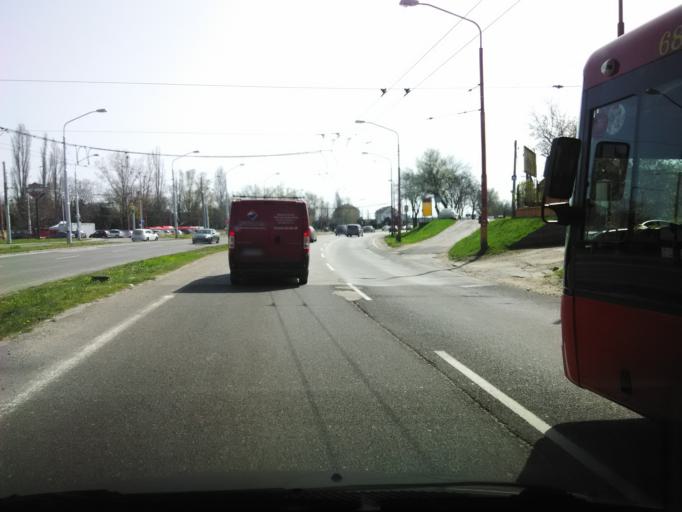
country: SK
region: Bratislavsky
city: Bratislava
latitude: 48.1440
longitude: 17.1889
